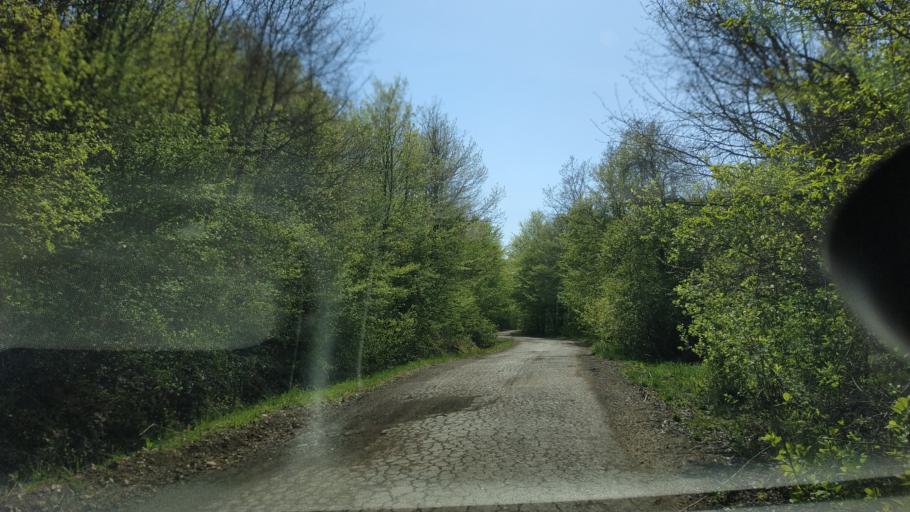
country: RS
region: Central Serbia
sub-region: Zajecarski Okrug
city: Soko Banja
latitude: 43.5071
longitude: 21.8985
